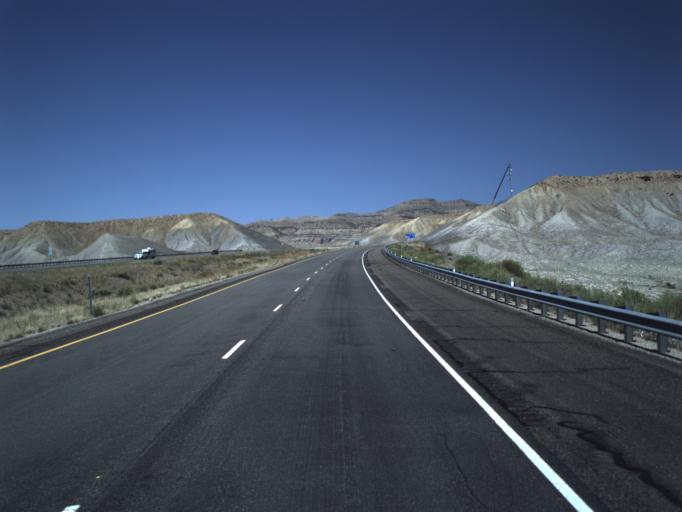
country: US
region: Utah
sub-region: Grand County
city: Moab
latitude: 38.9565
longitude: -109.7071
